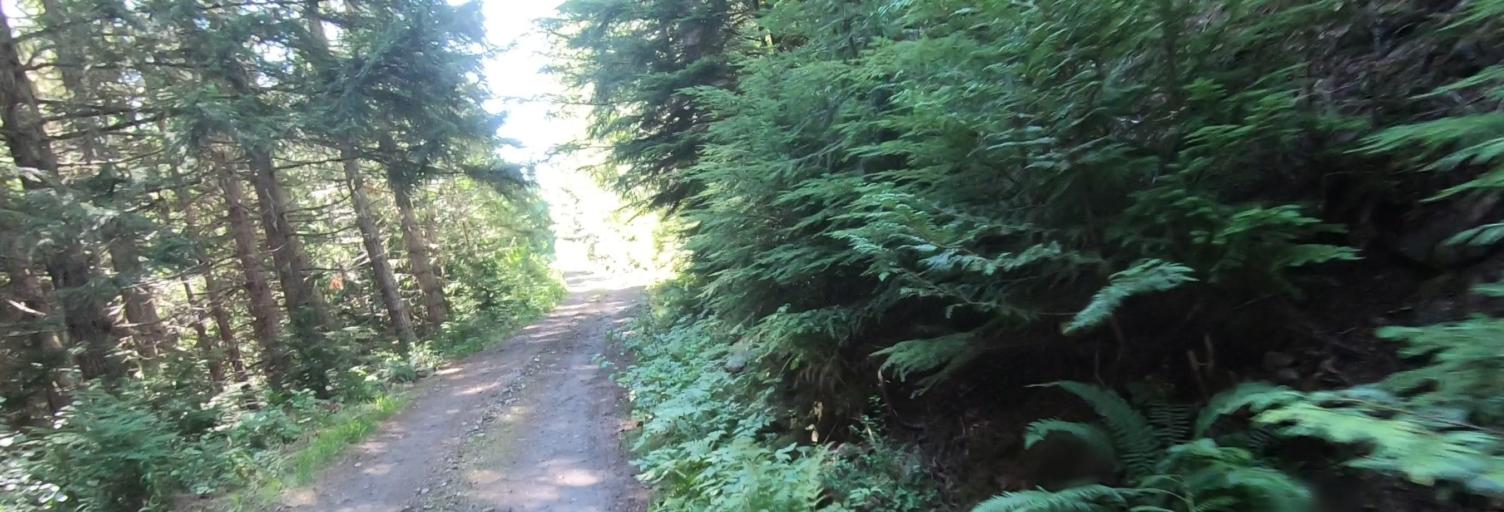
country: CA
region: British Columbia
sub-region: Fraser Valley Regional District
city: Chilliwack
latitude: 48.8634
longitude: -121.7787
